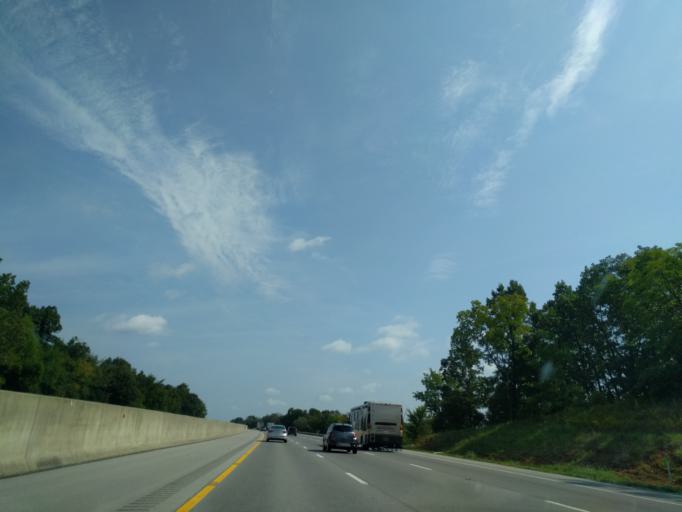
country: US
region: Kentucky
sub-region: Simpson County
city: Franklin
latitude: 36.7512
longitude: -86.4911
